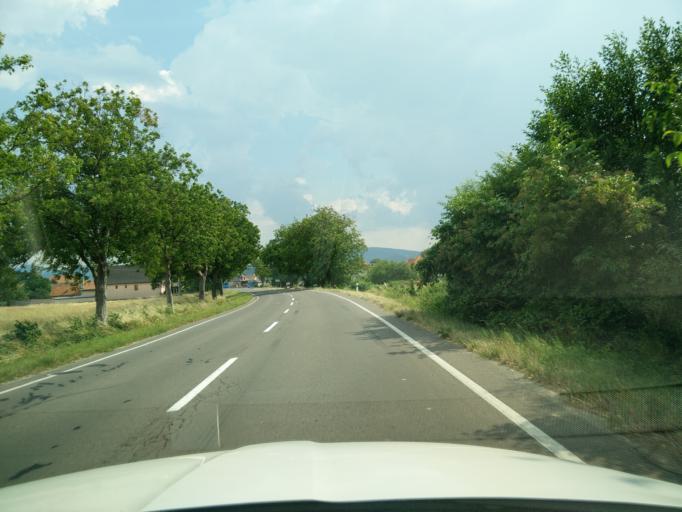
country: SK
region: Nitriansky
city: Novaky
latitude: 48.7524
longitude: 18.4971
